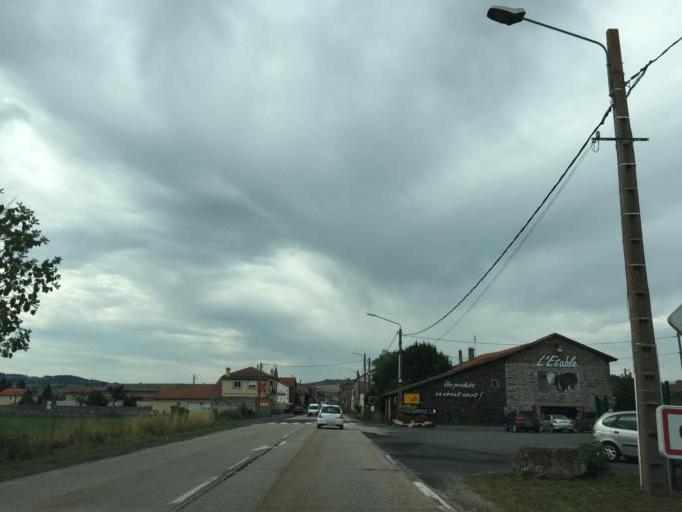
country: FR
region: Auvergne
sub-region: Departement de la Haute-Loire
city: Solignac-sur-Loire
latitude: 44.8981
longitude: 3.8505
